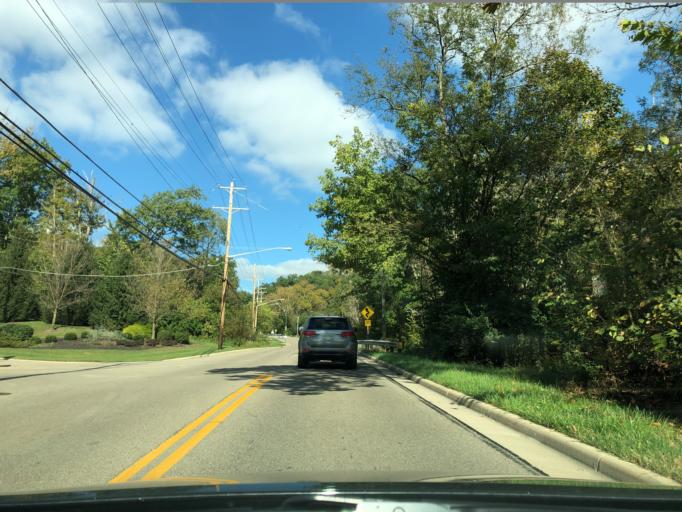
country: US
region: Ohio
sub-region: Hamilton County
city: Loveland
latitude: 39.2716
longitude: -84.2527
